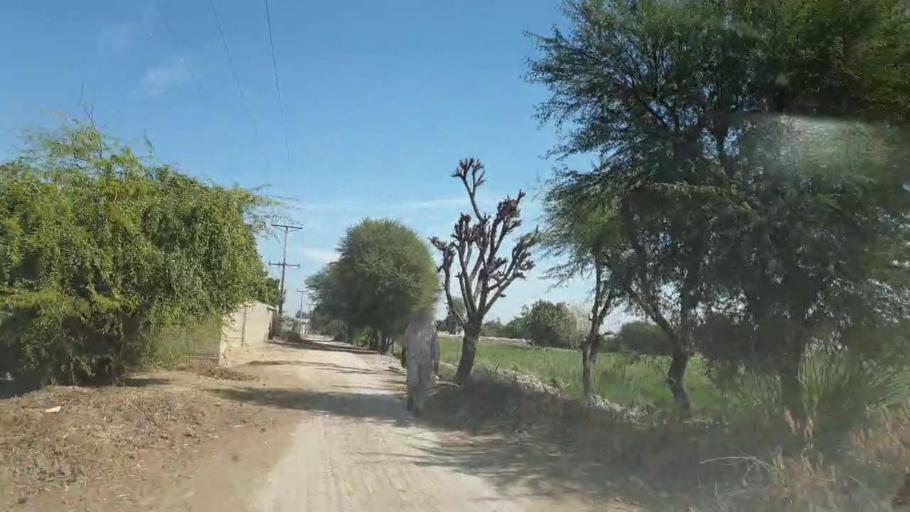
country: PK
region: Sindh
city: Pithoro
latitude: 25.6138
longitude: 69.2621
